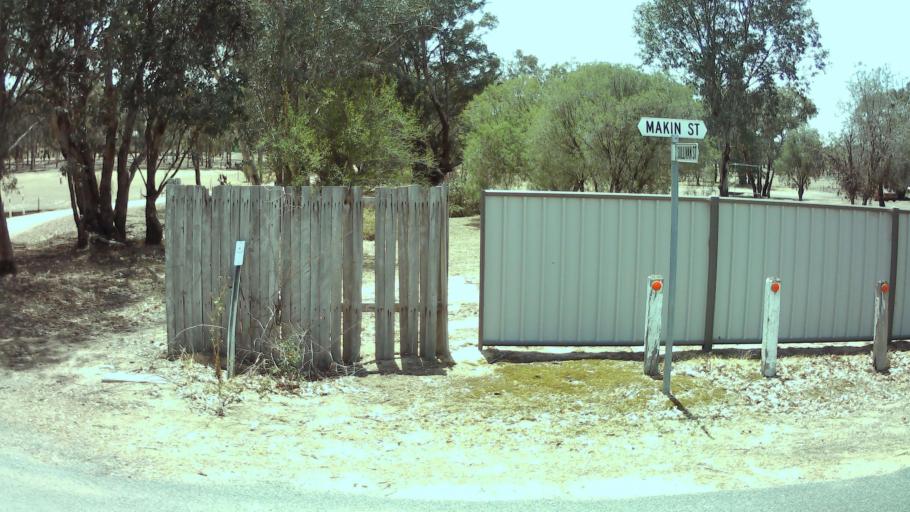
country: AU
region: New South Wales
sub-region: Weddin
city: Grenfell
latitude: -33.8885
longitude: 148.1695
